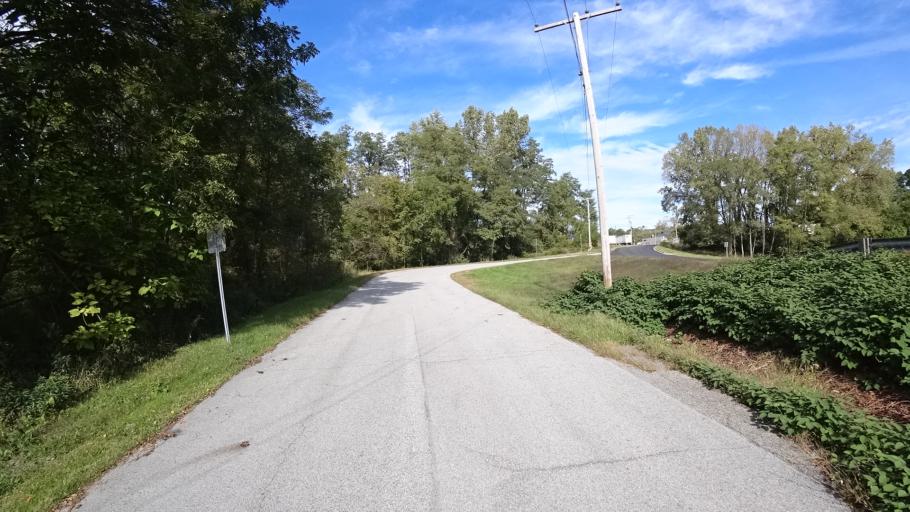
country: US
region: Indiana
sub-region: LaPorte County
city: Michigan City
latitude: 41.7230
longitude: -86.8759
